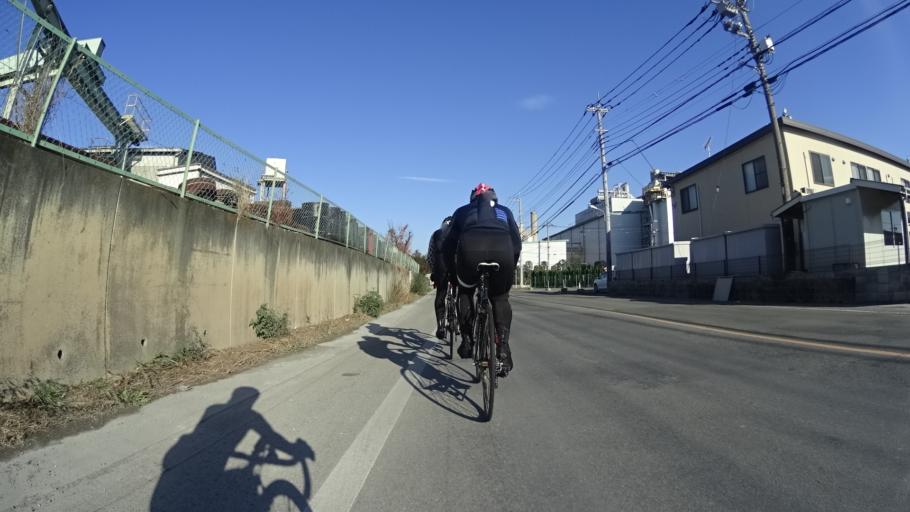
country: JP
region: Tokyo
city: Fussa
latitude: 35.7897
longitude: 139.3449
